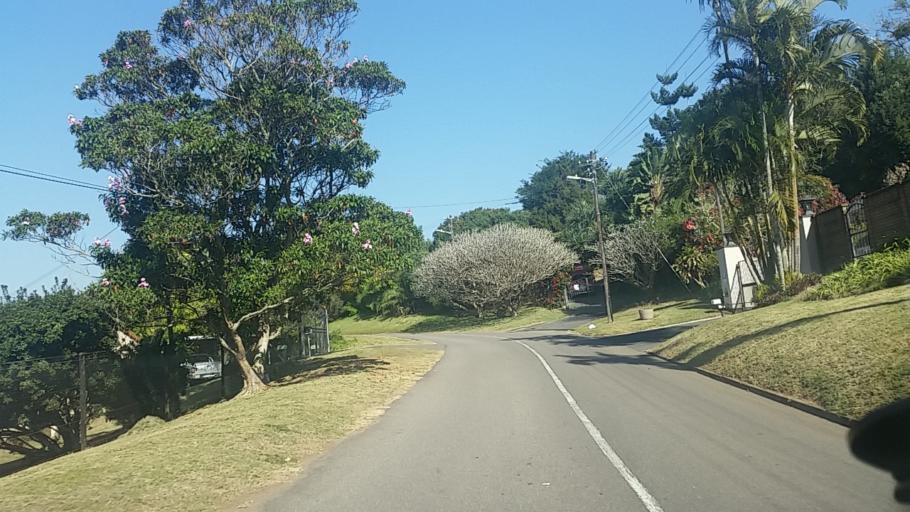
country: ZA
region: KwaZulu-Natal
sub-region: eThekwini Metropolitan Municipality
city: Berea
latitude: -29.8489
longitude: 30.9048
